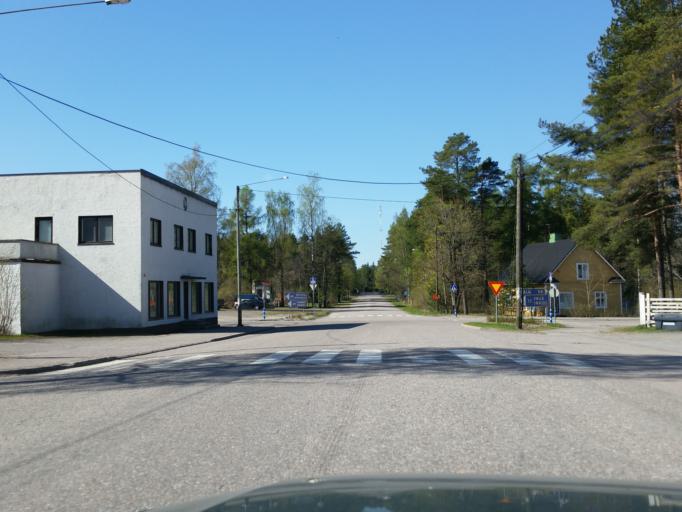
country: FI
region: Uusimaa
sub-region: Raaseporin
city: Inga
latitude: 60.1380
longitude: 23.8650
